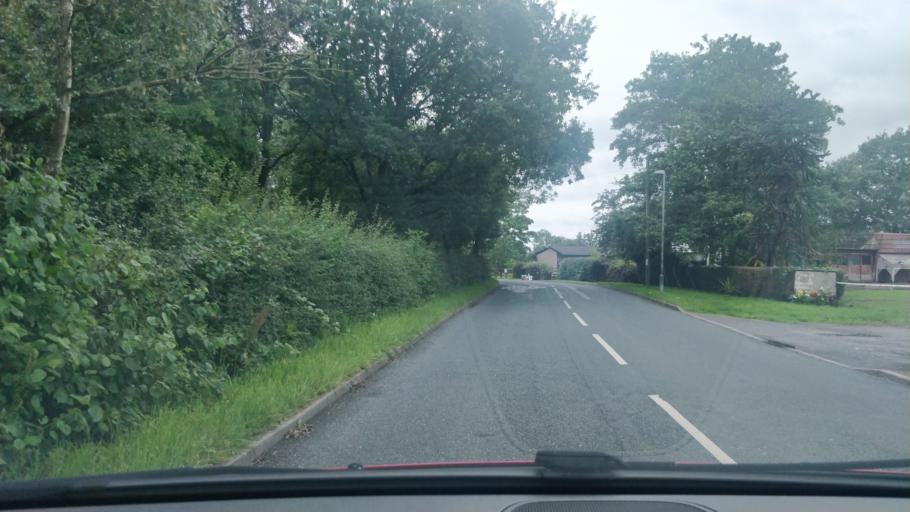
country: GB
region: England
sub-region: Lancashire
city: Croston
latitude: 53.7007
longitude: -2.7412
